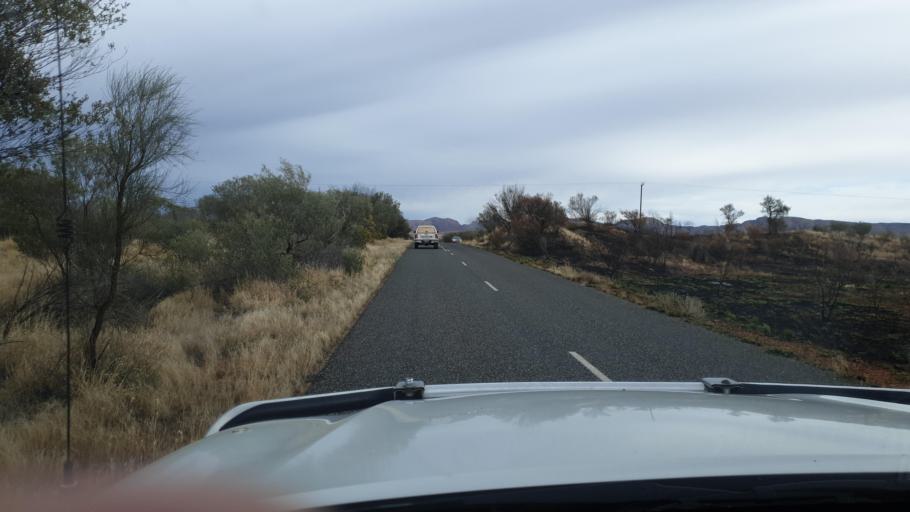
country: AU
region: Northern Territory
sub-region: Alice Springs
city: Alice Springs
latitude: -23.7856
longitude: 133.5135
